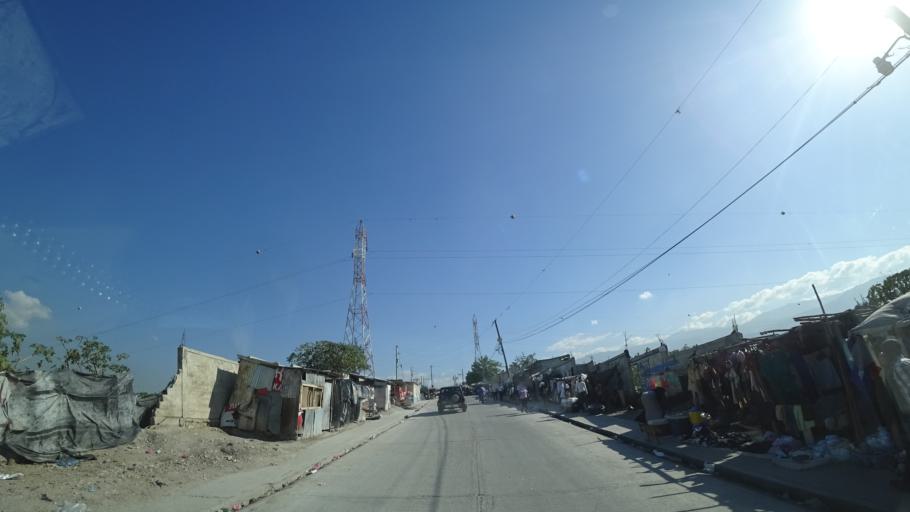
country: HT
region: Ouest
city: Delmas 73
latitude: 18.5633
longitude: -72.2877
